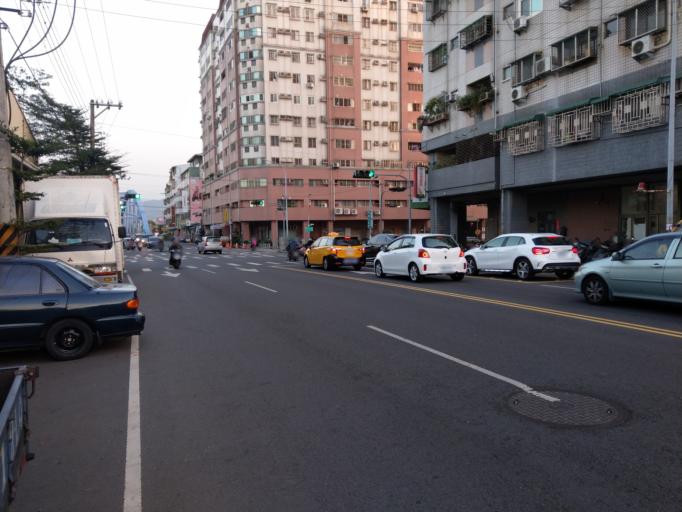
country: TW
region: Taiwan
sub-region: Taichung City
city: Taichung
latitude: 24.1600
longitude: 120.7017
